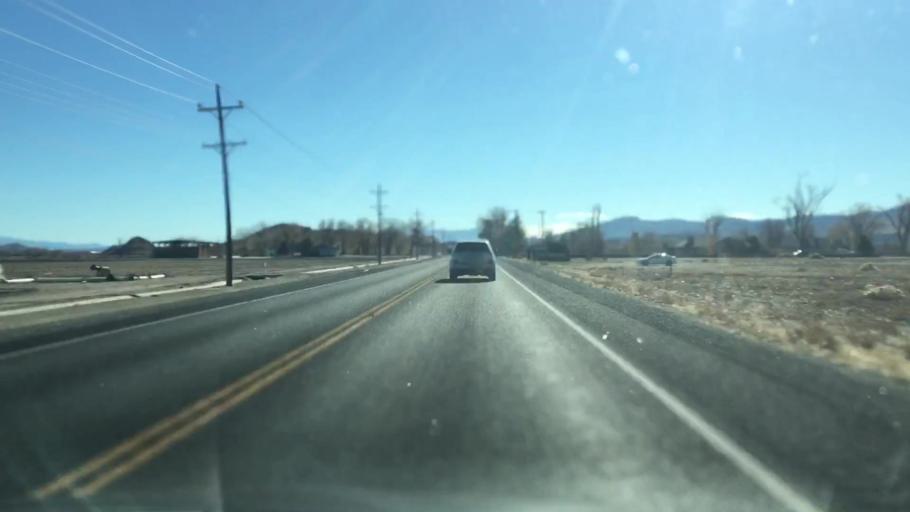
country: US
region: Nevada
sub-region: Lyon County
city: Yerington
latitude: 39.0357
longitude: -119.1816
